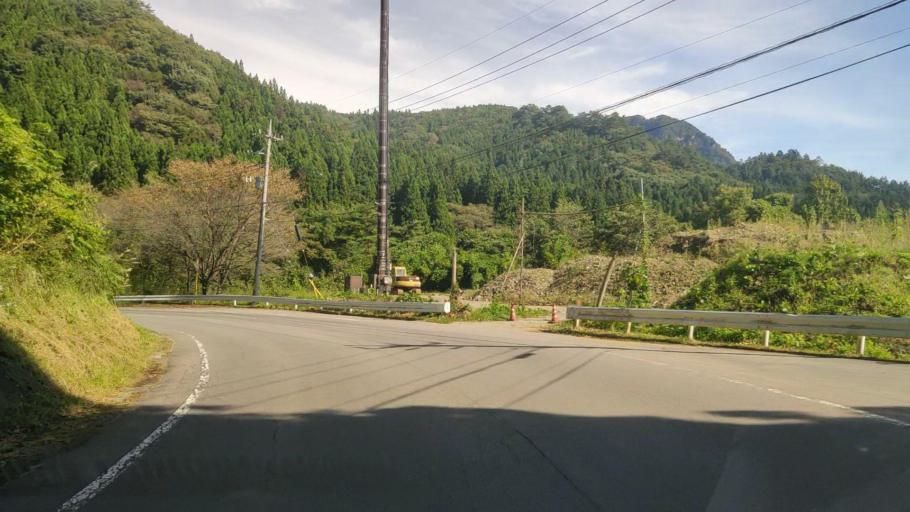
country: JP
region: Gunma
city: Nakanojomachi
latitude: 36.6029
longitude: 138.7132
